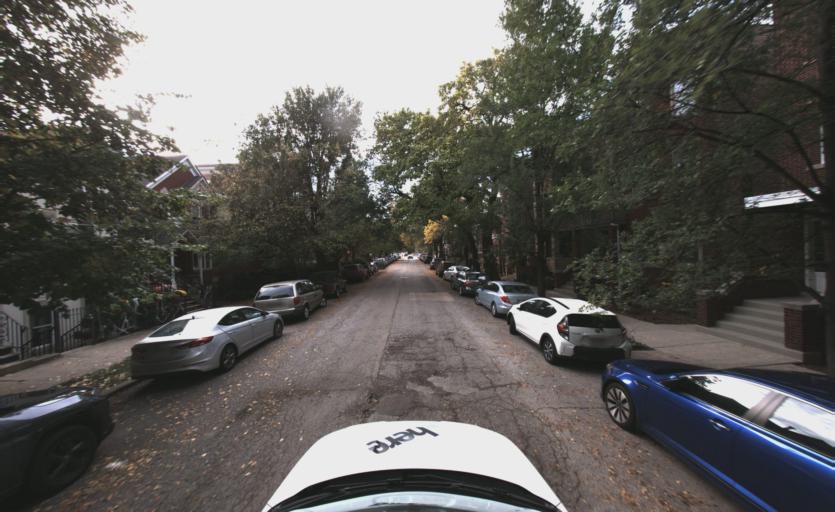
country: US
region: Illinois
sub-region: Cook County
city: Chicago
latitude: 41.9242
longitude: -87.6858
